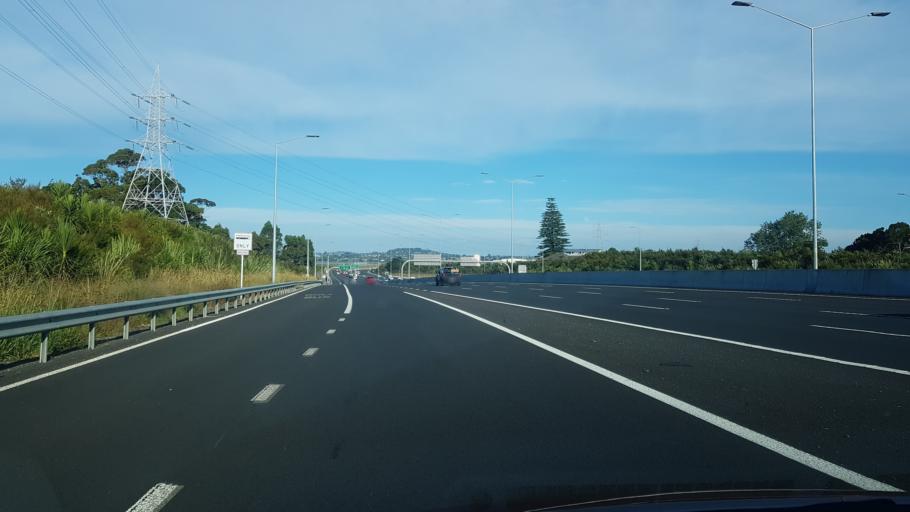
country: NZ
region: Auckland
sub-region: Auckland
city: Rosebank
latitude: -36.8579
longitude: 174.6538
